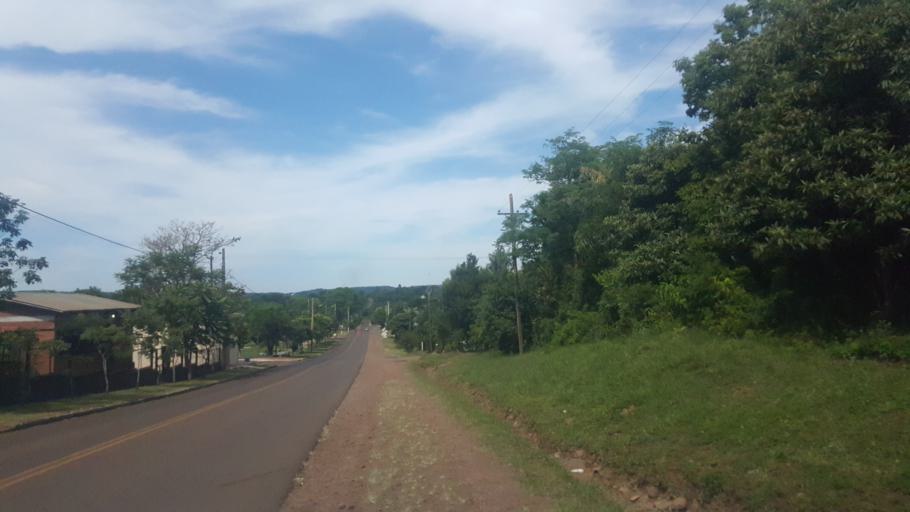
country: AR
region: Misiones
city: Cerro Cora
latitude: -27.5130
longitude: -55.6104
